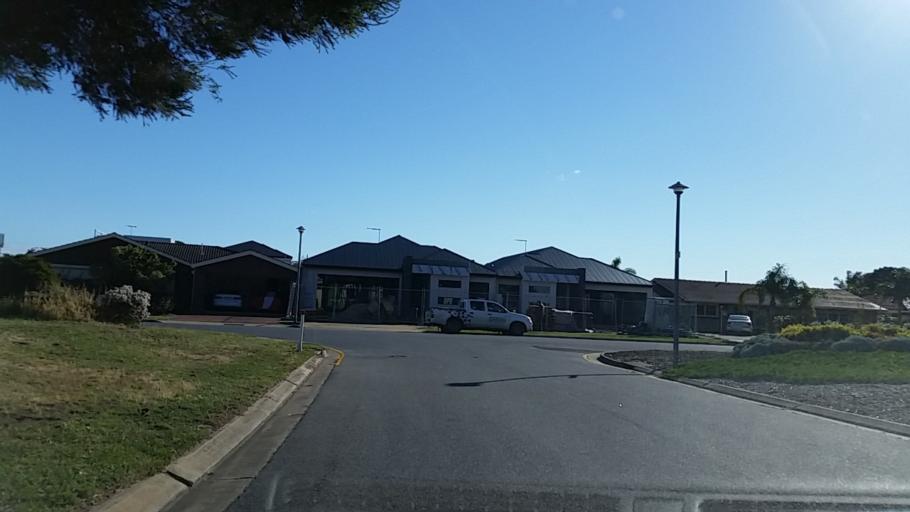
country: AU
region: South Australia
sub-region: Charles Sturt
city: Royal Park
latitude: -34.8731
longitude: 138.5004
